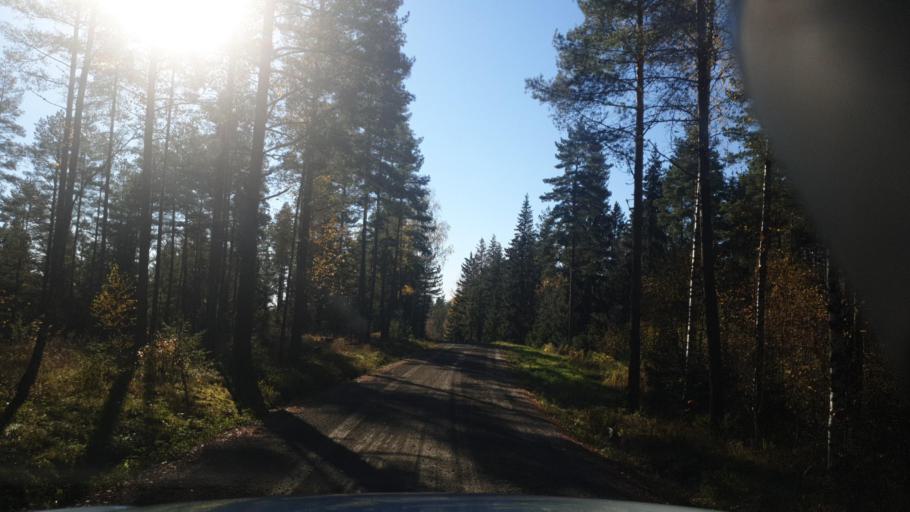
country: SE
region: Vaermland
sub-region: Grums Kommun
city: Grums
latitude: 59.4663
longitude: 12.9213
